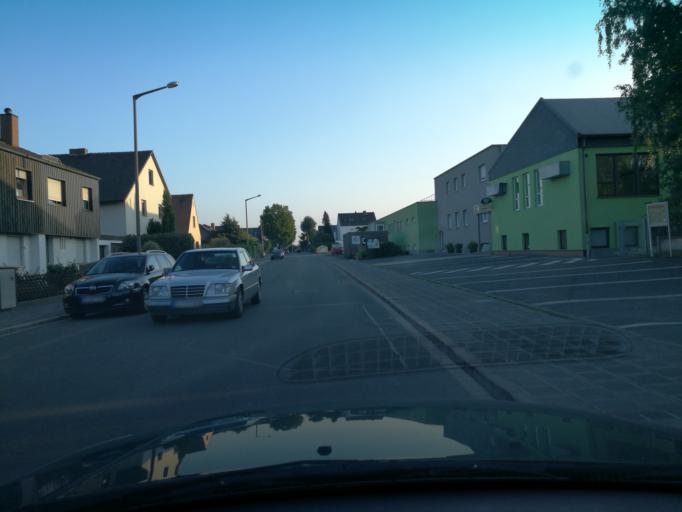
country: DE
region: Bavaria
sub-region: Regierungsbezirk Mittelfranken
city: Wetzendorf
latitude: 49.4754
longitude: 11.0215
